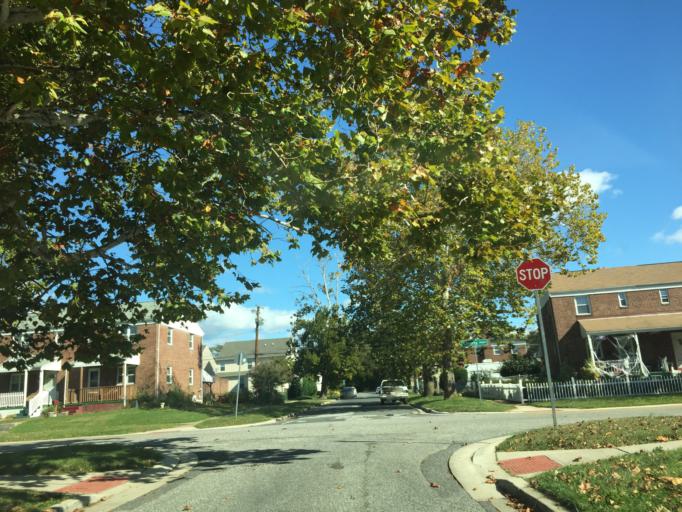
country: US
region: Maryland
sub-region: Baltimore County
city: Dundalk
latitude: 39.2623
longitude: -76.5194
